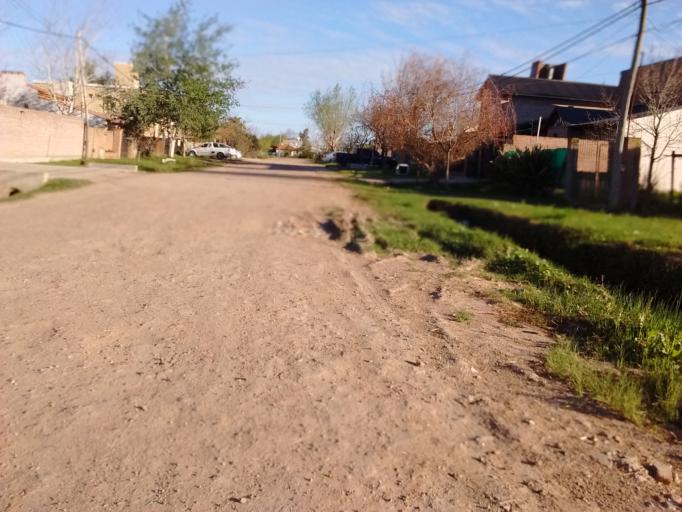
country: AR
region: Santa Fe
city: Funes
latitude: -32.9244
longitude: -60.7936
